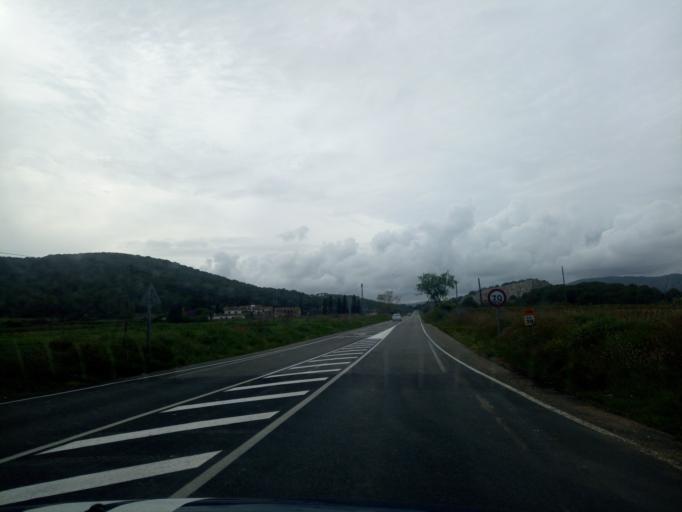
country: ES
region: Catalonia
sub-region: Provincia de Barcelona
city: Sitges
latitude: 41.2330
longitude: 1.7836
